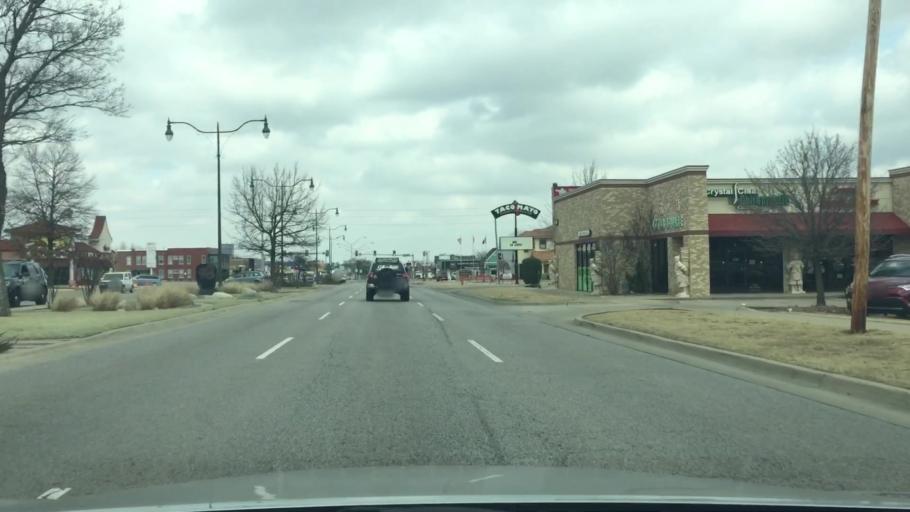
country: US
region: Oklahoma
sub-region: Oklahoma County
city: Oklahoma City
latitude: 35.4986
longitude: -97.5342
